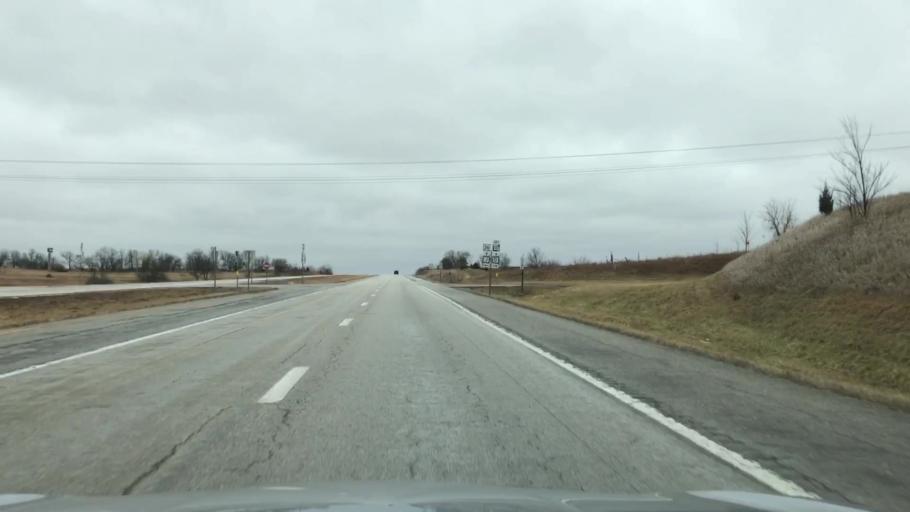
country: US
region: Missouri
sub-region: Caldwell County
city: Hamilton
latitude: 39.7502
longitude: -94.1126
